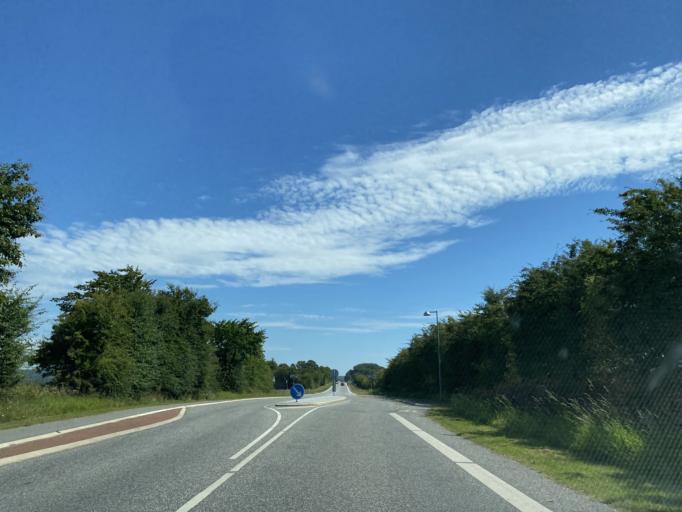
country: DK
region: South Denmark
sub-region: Faaborg-Midtfyn Kommune
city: Faaborg
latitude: 55.1092
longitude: 10.1773
